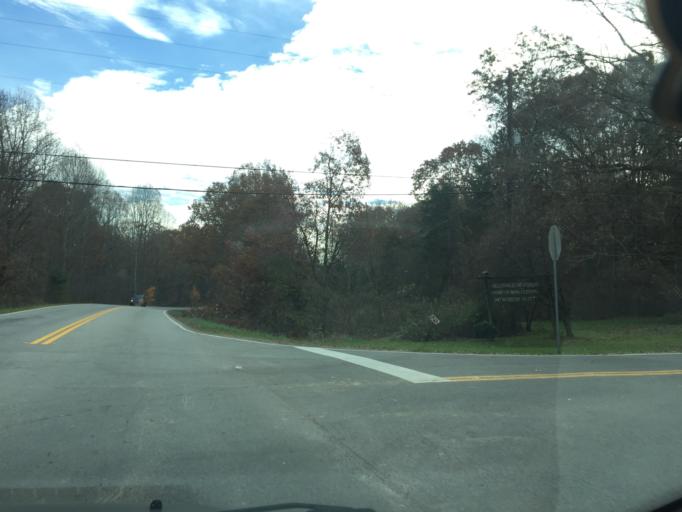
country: US
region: Georgia
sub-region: Dade County
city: Trenton
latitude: 34.8246
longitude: -85.5020
